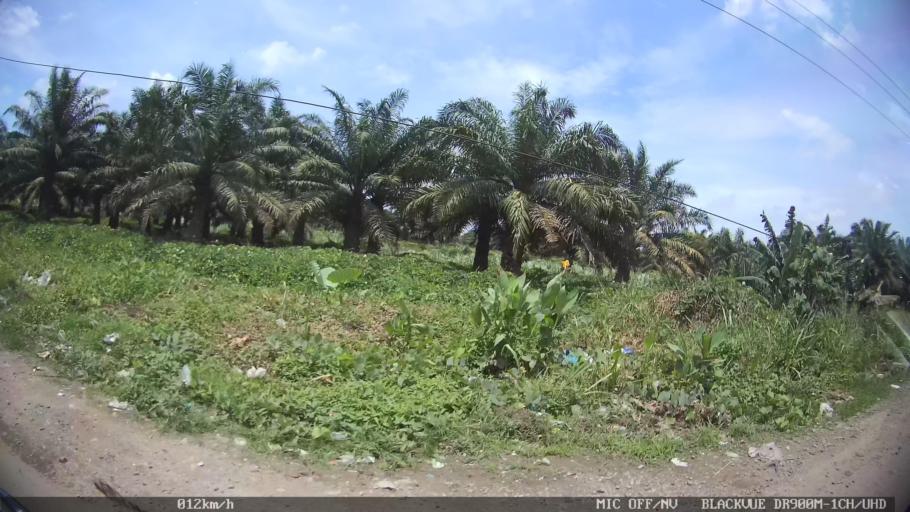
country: ID
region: North Sumatra
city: Perbaungan
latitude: 3.5329
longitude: 98.8860
